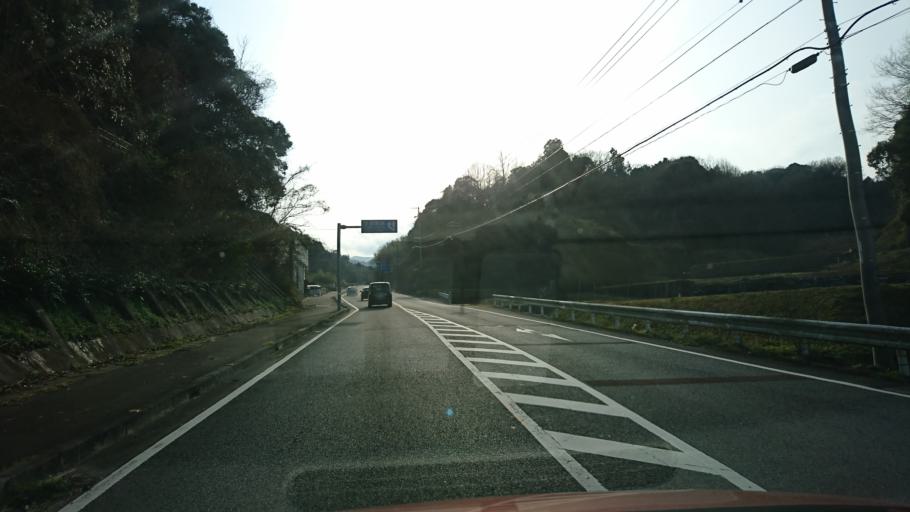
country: JP
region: Ehime
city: Hojo
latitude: 34.0014
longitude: 132.9373
